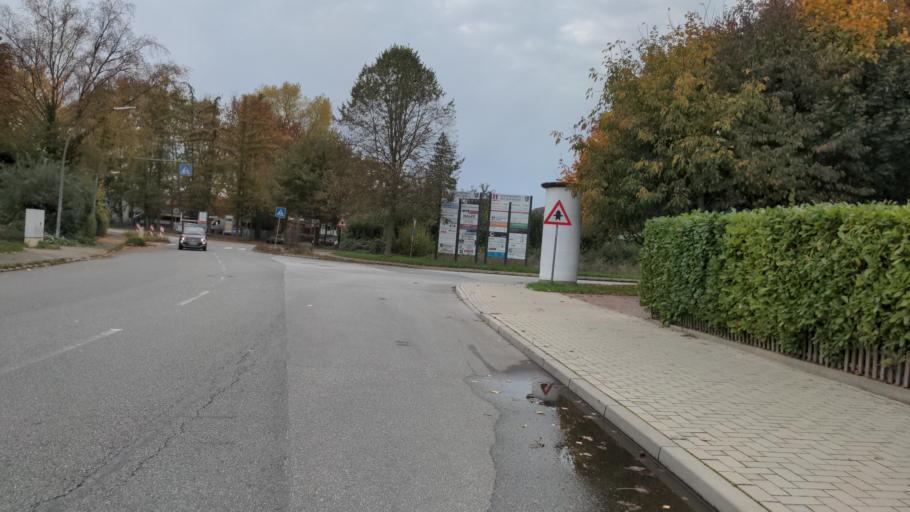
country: DE
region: Schleswig-Holstein
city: Bad Schwartau
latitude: 53.9114
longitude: 10.6739
